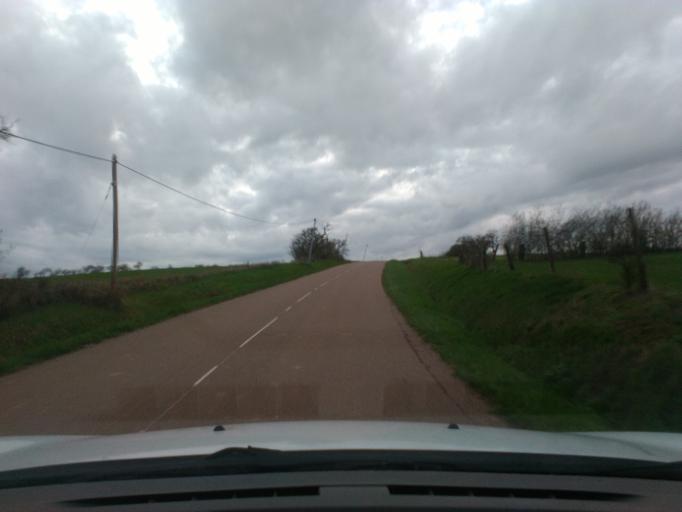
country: FR
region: Lorraine
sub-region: Departement des Vosges
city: Mirecourt
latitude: 48.3529
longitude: 6.0783
